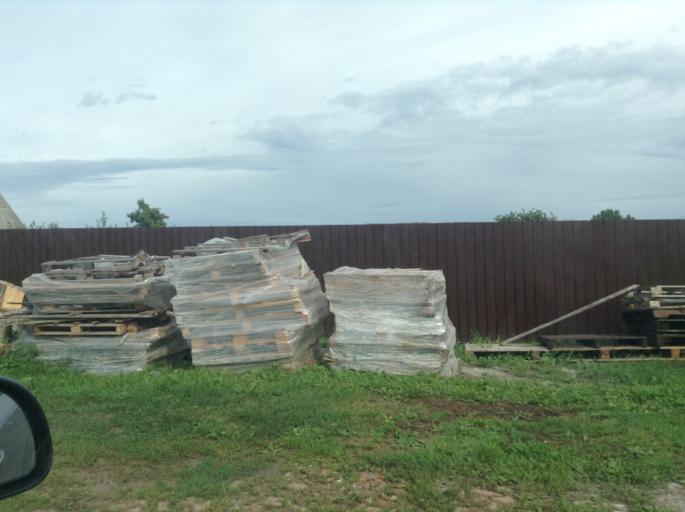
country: RU
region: Moskovskaya
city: Yegor'yevsk
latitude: 55.3628
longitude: 39.0964
